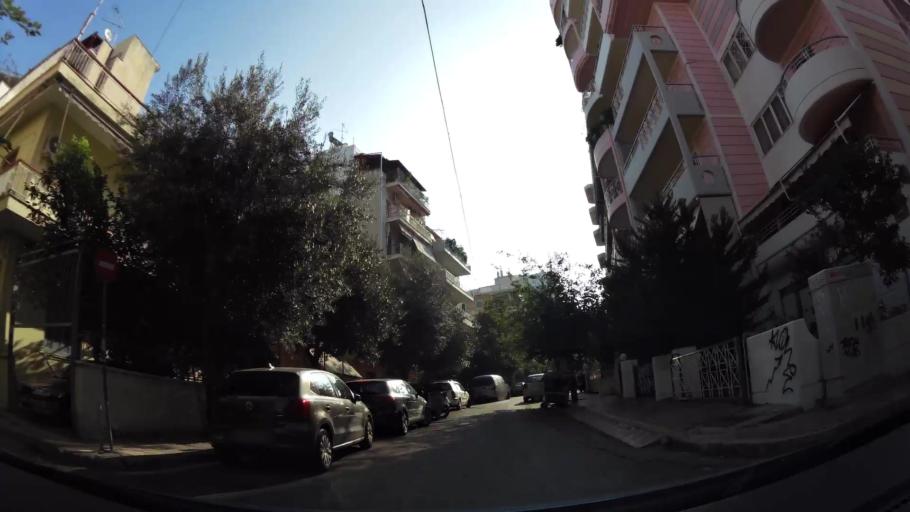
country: GR
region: Attica
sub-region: Nomarchia Athinas
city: Kaisariani
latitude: 37.9734
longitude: 23.7731
